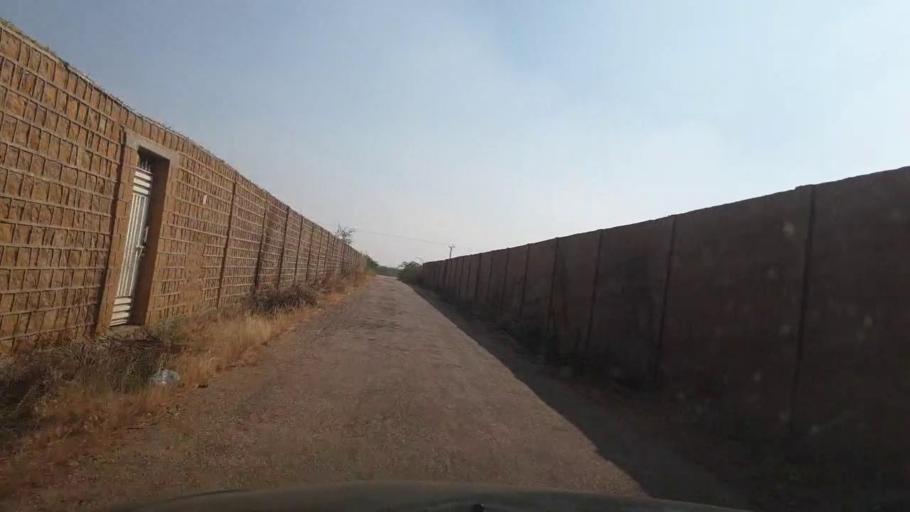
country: PK
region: Sindh
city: Jamshoro
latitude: 25.4072
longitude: 67.7887
